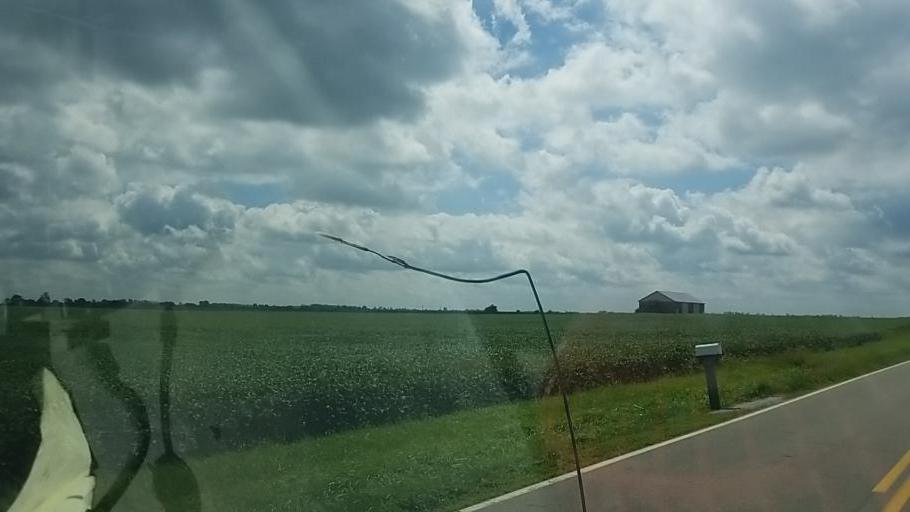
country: US
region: Ohio
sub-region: Fayette County
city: Jeffersonville
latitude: 39.6839
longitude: -83.5037
